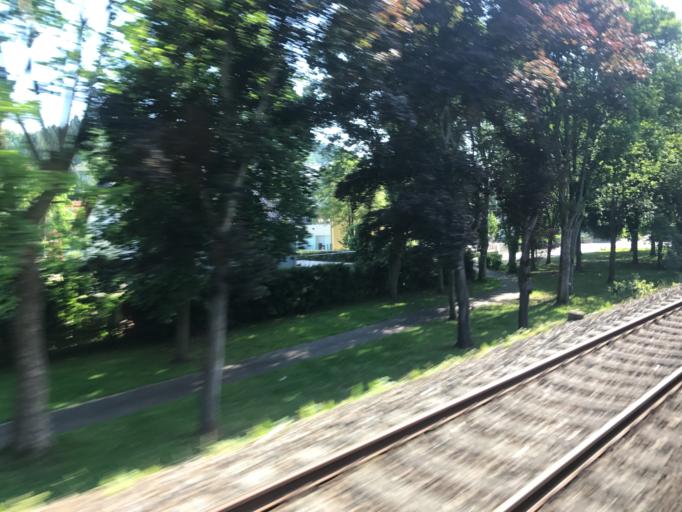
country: DE
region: Rheinland-Pfalz
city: Staudernheim
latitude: 49.7823
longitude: 7.6603
